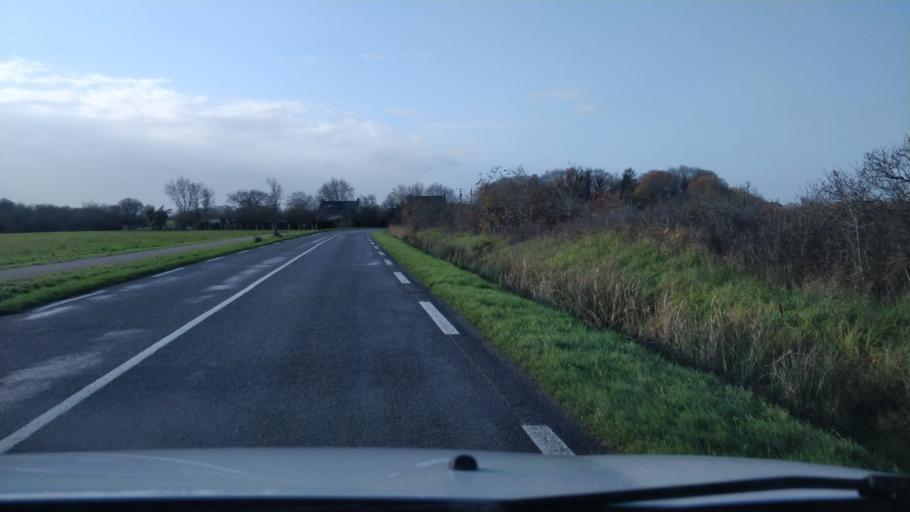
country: FR
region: Pays de la Loire
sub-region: Departement de la Loire-Atlantique
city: Asserac
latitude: 47.4053
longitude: -2.4000
